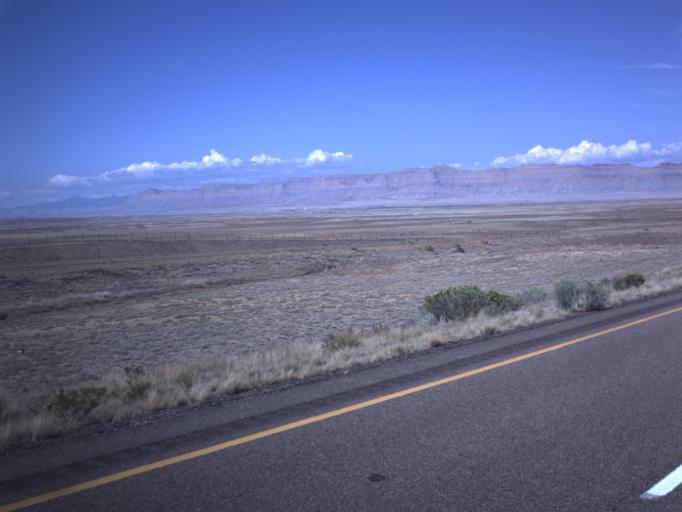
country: US
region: Utah
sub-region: Carbon County
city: East Carbon City
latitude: 38.9436
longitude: -110.3284
